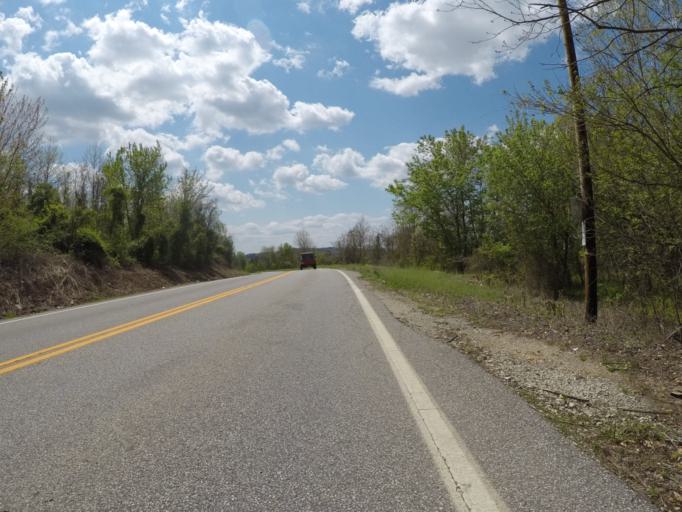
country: US
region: West Virginia
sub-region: Cabell County
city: Pea Ridge
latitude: 38.4508
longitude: -82.3763
